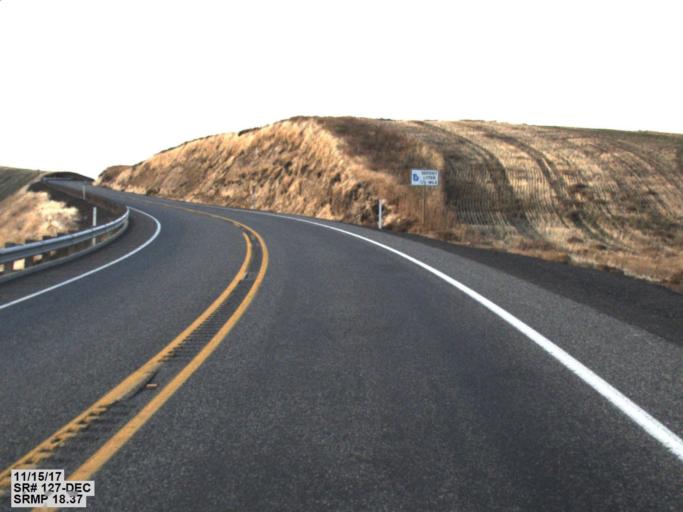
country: US
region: Washington
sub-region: Garfield County
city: Pomeroy
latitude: 46.7233
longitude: -117.7679
